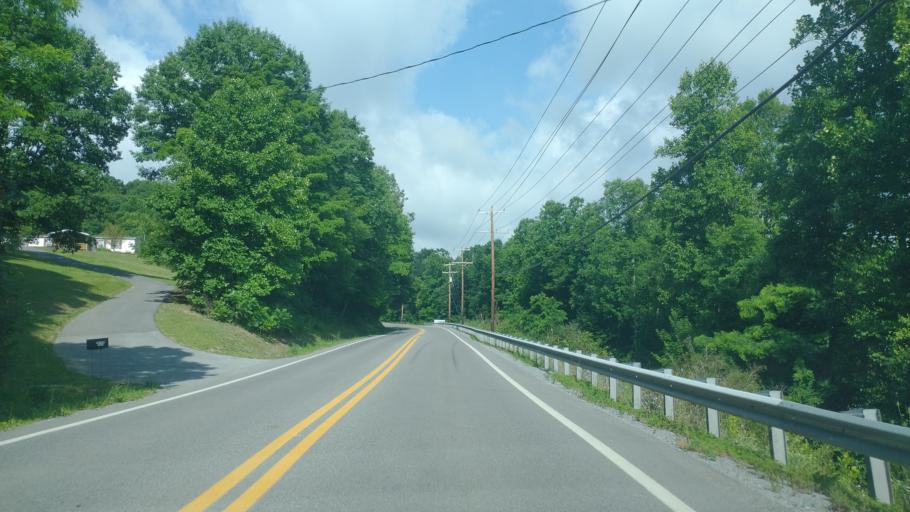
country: US
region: West Virginia
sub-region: Mercer County
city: Princeton
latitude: 37.3604
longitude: -81.1313
